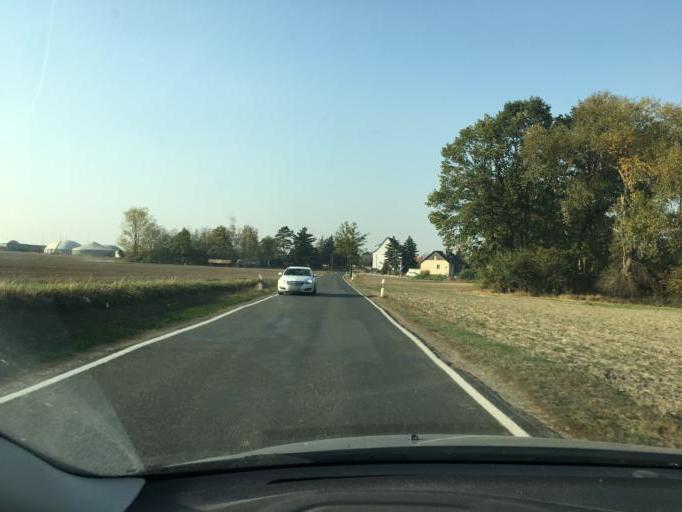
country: DE
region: Saxony
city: Wurzen
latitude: 51.3394
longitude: 12.7698
